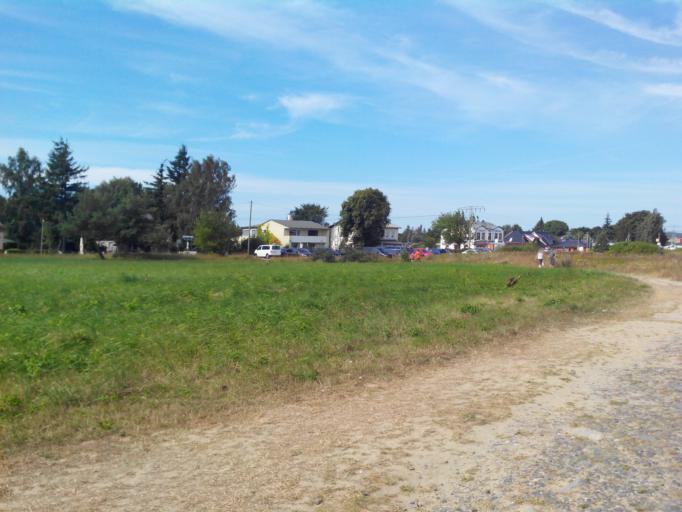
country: DE
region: Mecklenburg-Vorpommern
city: Sagard
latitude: 54.4794
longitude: 13.5774
